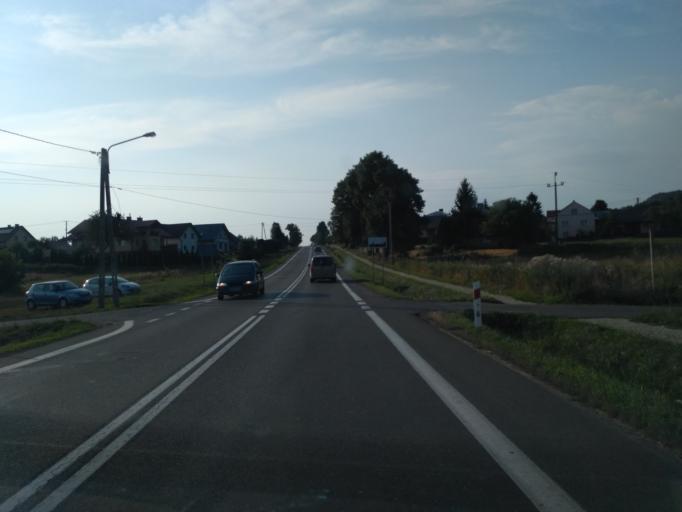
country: PL
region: Subcarpathian Voivodeship
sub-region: Powiat brzozowski
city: Stara Wies
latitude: 49.7375
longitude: 21.9936
